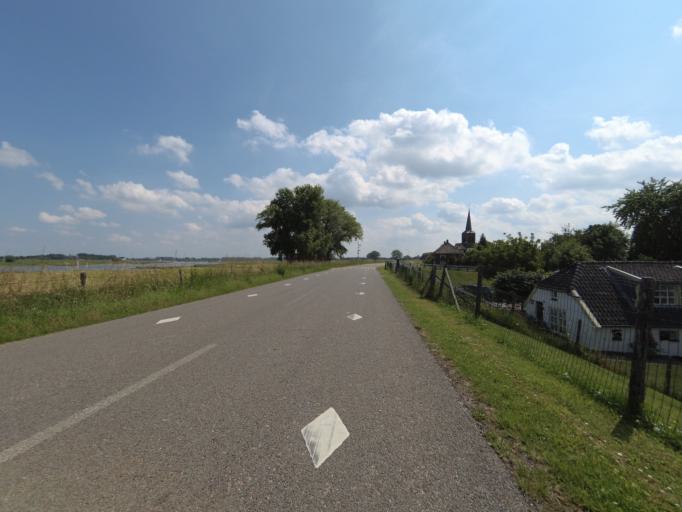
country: NL
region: Utrecht
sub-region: Gemeente Wijk bij Duurstede
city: Wijk bij Duurstede
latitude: 51.9535
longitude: 5.3265
